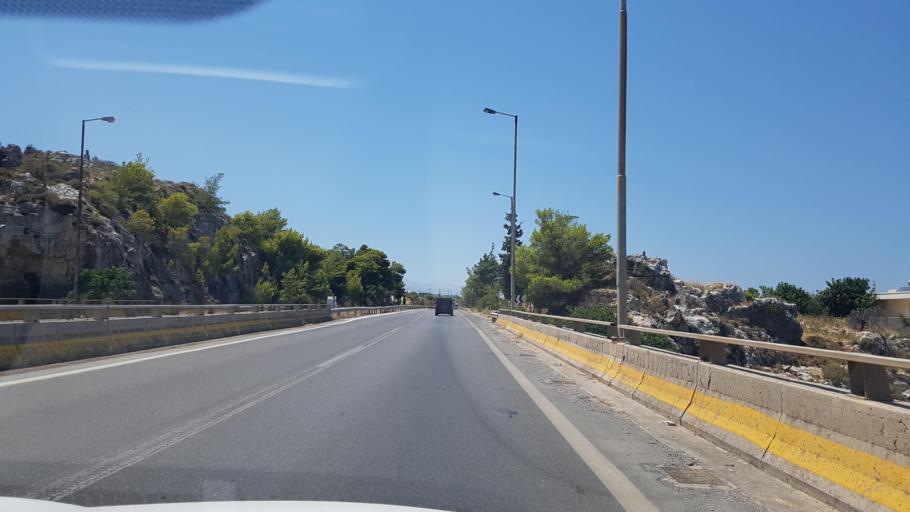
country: GR
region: Crete
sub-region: Nomos Rethymnis
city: Rethymno
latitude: 35.3558
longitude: 24.4766
